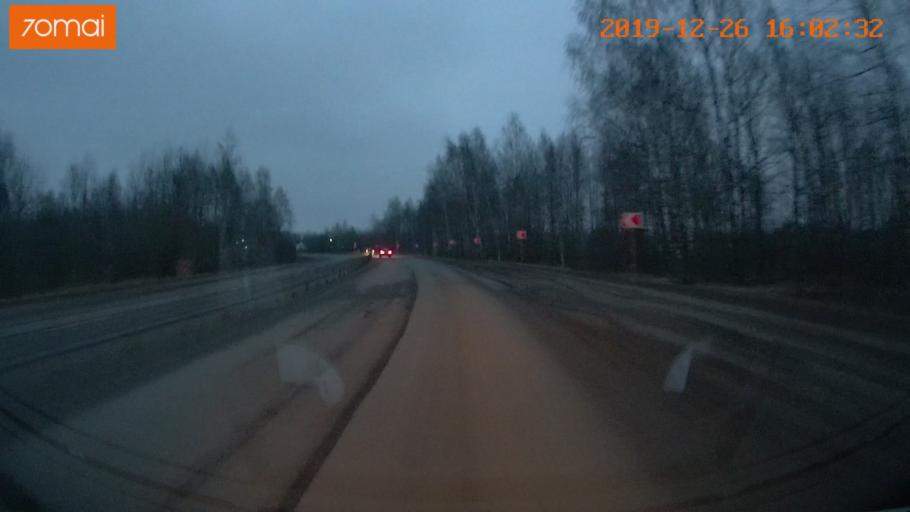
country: RU
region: Jaroslavl
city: Rybinsk
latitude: 58.0110
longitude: 38.8368
